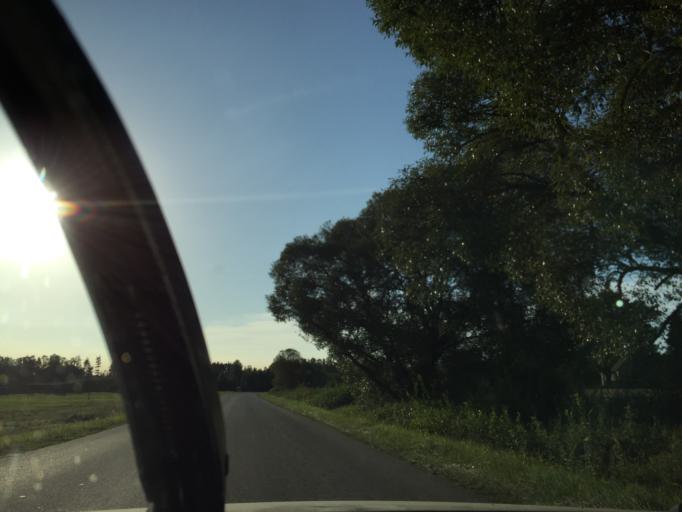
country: LT
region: Panevezys
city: Rokiskis
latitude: 55.9029
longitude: 25.6558
